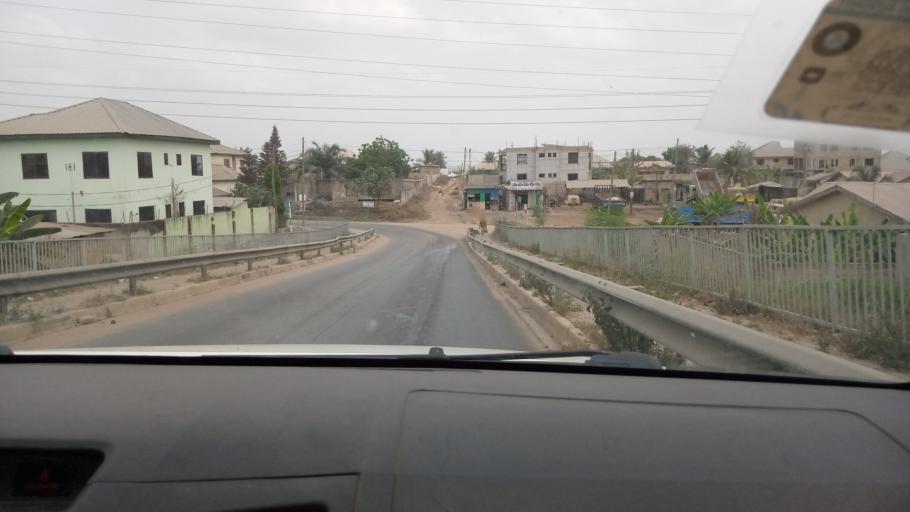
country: GH
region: Central
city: Kasoa
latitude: 5.5298
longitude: -0.4494
